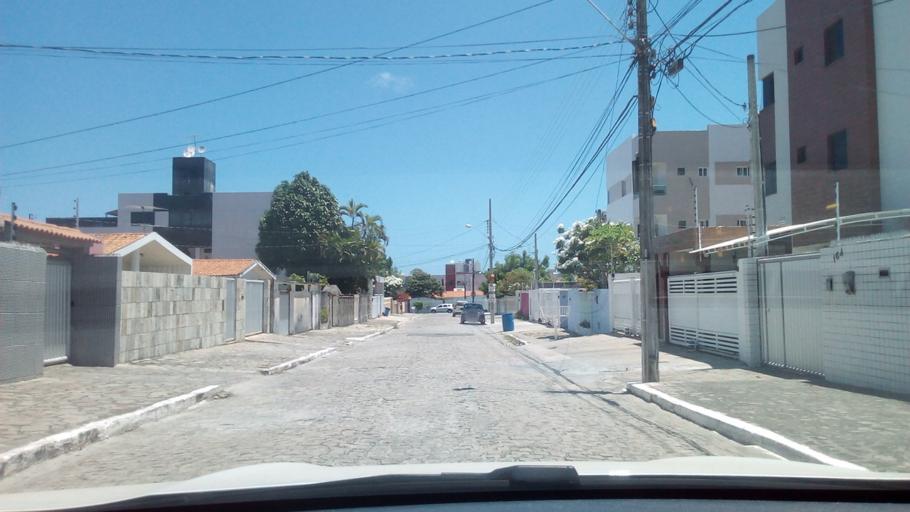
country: BR
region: Paraiba
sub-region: Joao Pessoa
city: Joao Pessoa
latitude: -7.1462
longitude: -34.8416
